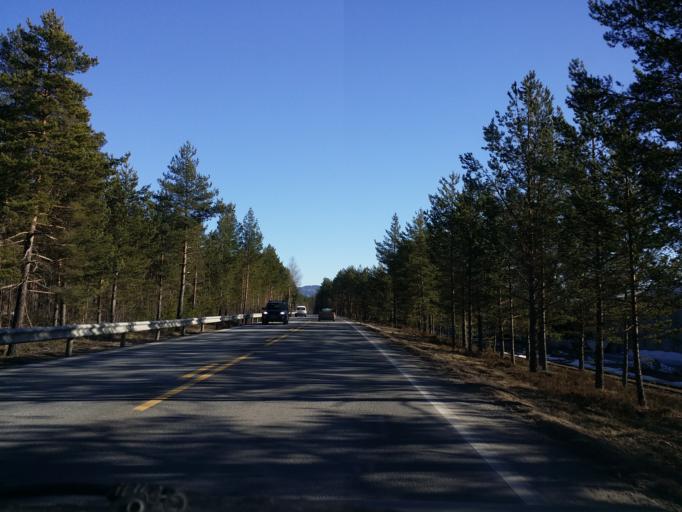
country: NO
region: Buskerud
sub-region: Ringerike
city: Honefoss
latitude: 60.2280
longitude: 10.2426
